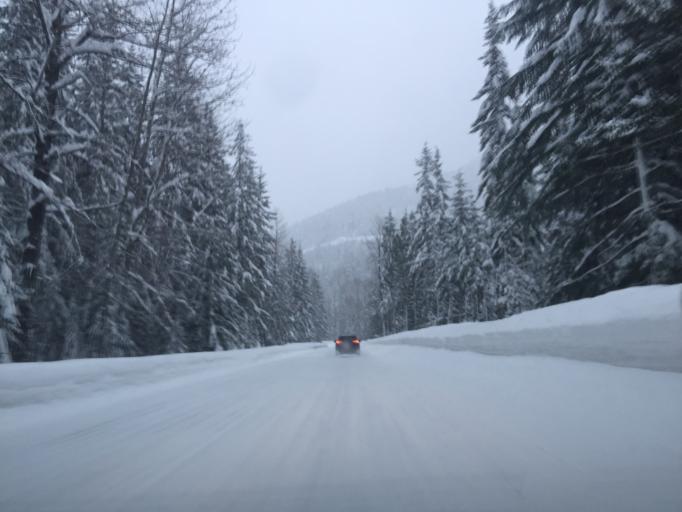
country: US
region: Washington
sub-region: Chelan County
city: Leavenworth
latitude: 47.7745
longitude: -121.0174
